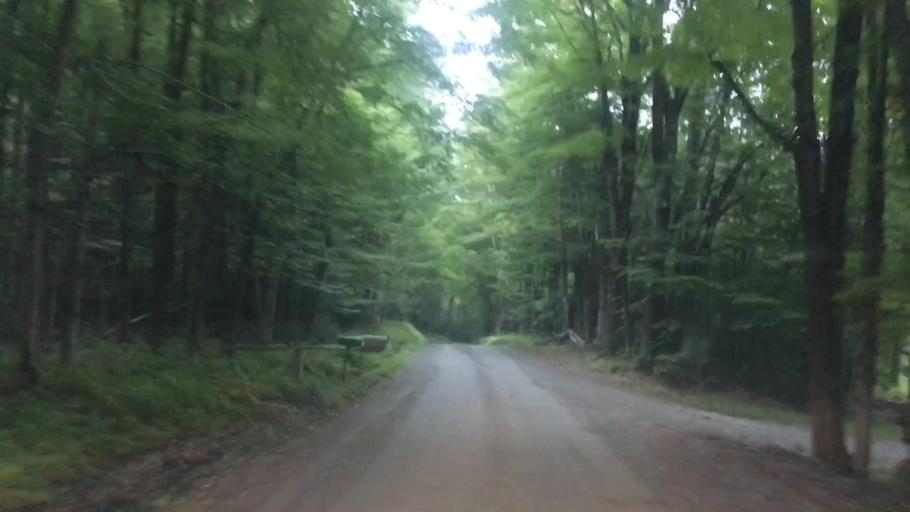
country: US
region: Vermont
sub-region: Windham County
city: Dover
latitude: 42.8401
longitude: -72.7676
